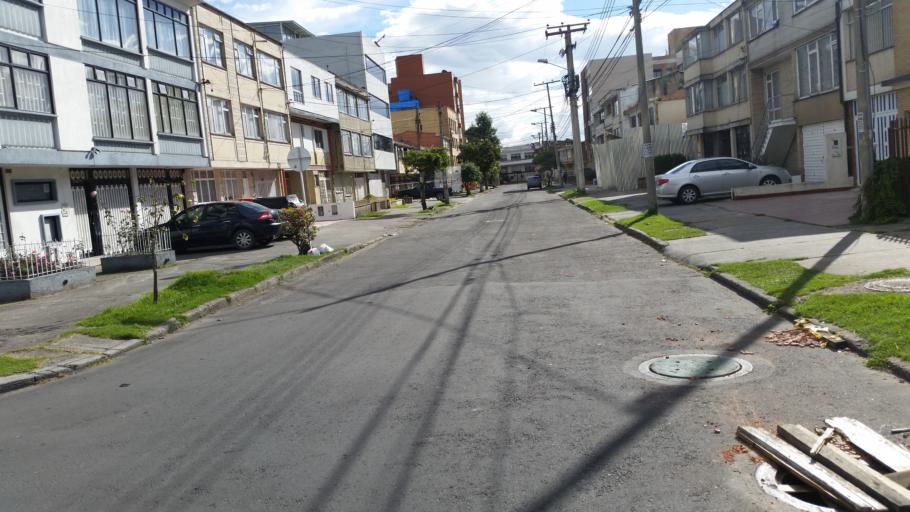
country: CO
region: Bogota D.C.
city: Bogota
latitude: 4.6277
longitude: -74.0834
